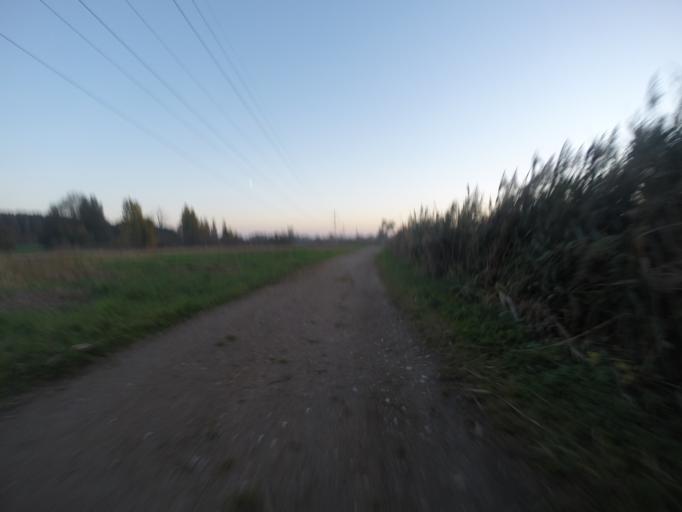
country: DK
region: Capital Region
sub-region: Hoje-Taastrup Kommune
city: Taastrup
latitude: 55.6666
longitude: 12.3196
